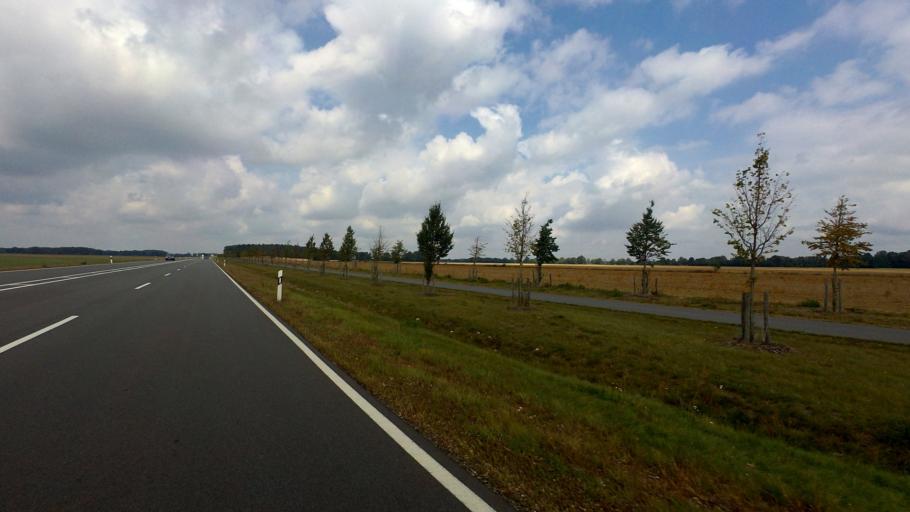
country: DE
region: Brandenburg
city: Herzberg
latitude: 51.6638
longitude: 13.2791
